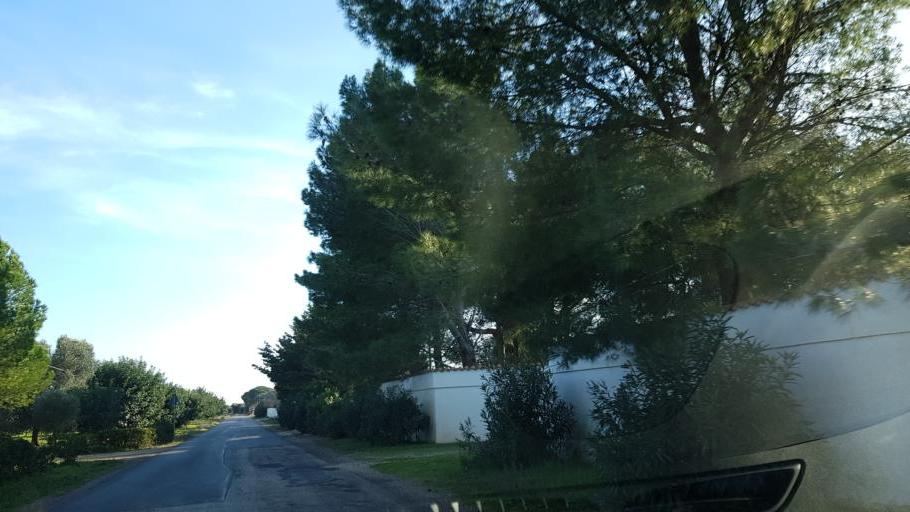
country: IT
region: Apulia
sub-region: Provincia di Brindisi
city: San Vito dei Normanni
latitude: 40.6750
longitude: 17.7763
